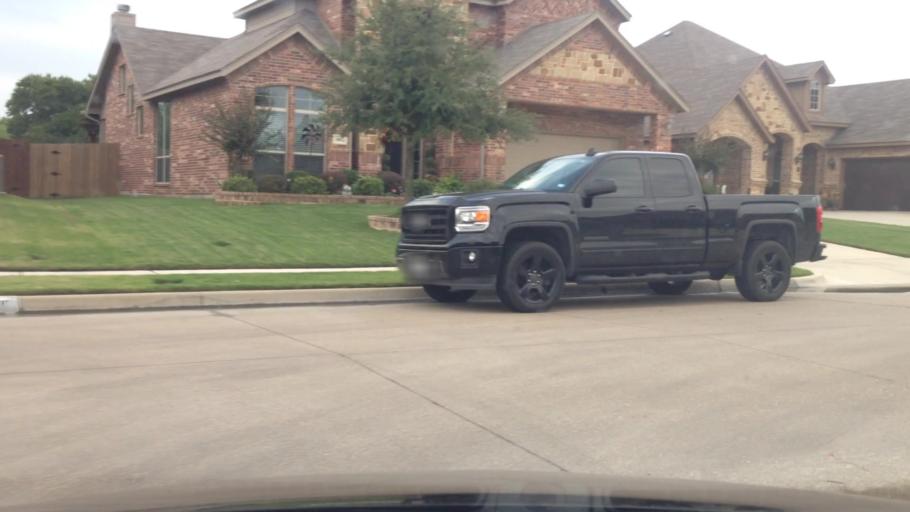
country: US
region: Texas
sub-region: Johnson County
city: Burleson
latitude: 32.5689
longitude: -97.3329
